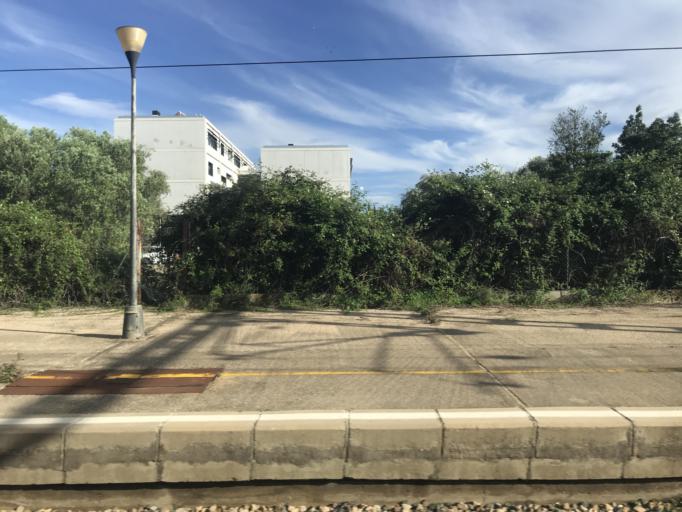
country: ES
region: Valencia
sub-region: Provincia de Castello
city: Vinaros
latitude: 40.4706
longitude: 0.4544
